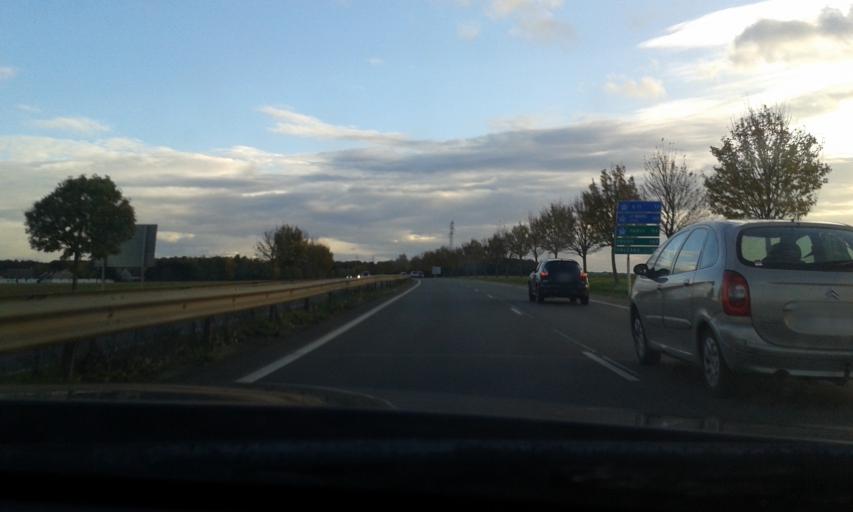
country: FR
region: Centre
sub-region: Departement d'Eure-et-Loir
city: Mainvilliers
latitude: 48.4340
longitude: 1.4310
